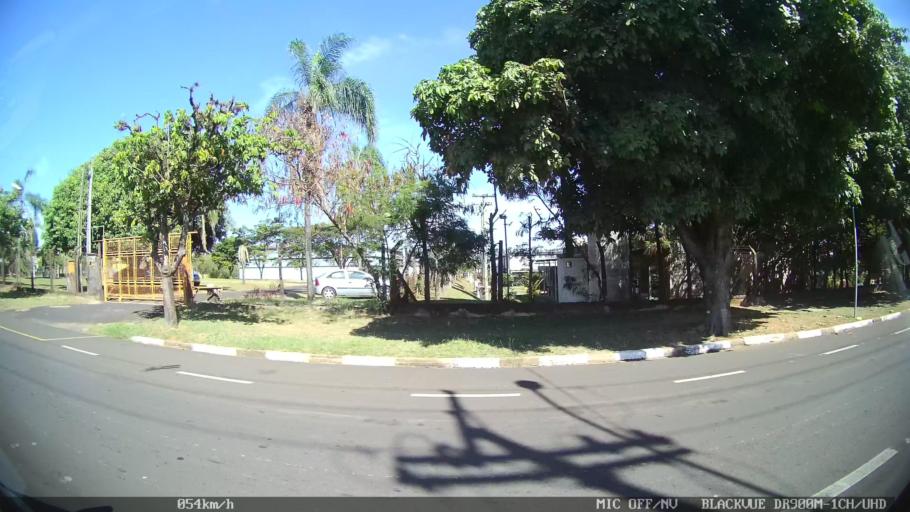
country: BR
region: Sao Paulo
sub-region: Franca
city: Franca
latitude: -20.5528
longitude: -47.4441
